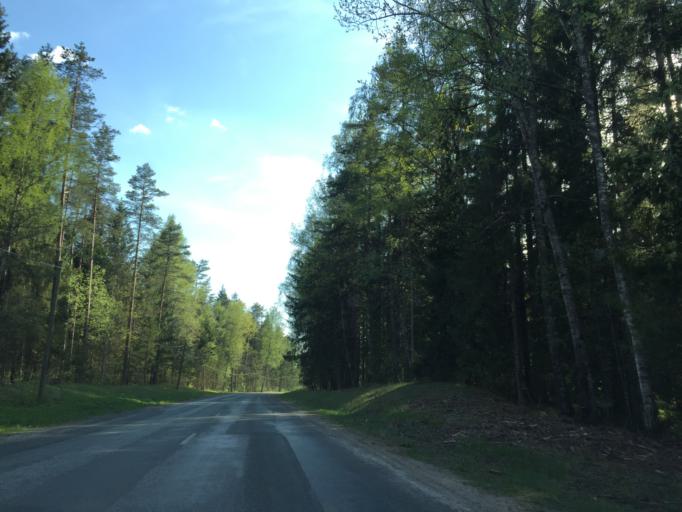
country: LV
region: Sigulda
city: Sigulda
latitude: 57.2410
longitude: 24.8599
